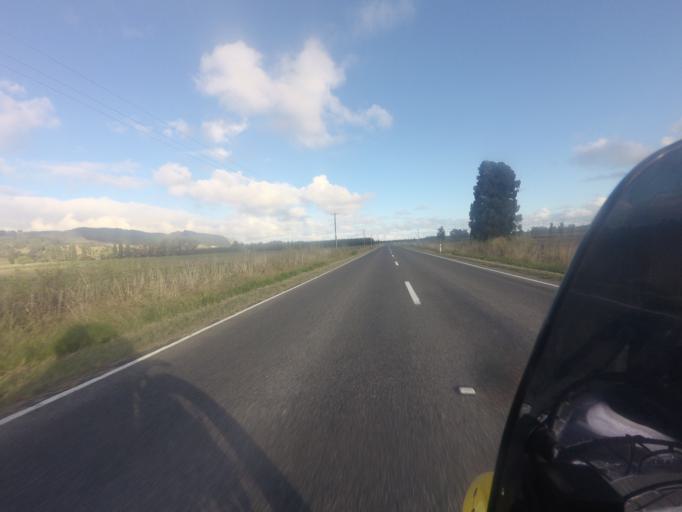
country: NZ
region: Gisborne
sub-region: Gisborne District
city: Gisborne
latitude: -38.5843
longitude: 177.9427
